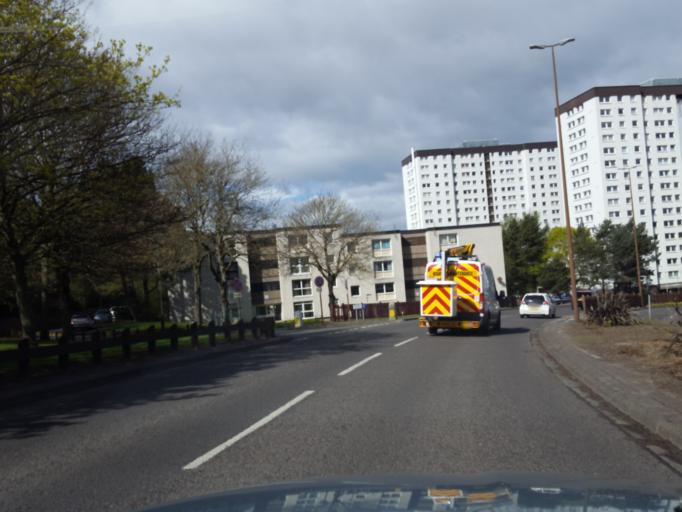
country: GB
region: Scotland
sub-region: Dundee City
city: Dundee
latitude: 56.4704
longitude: -3.0101
